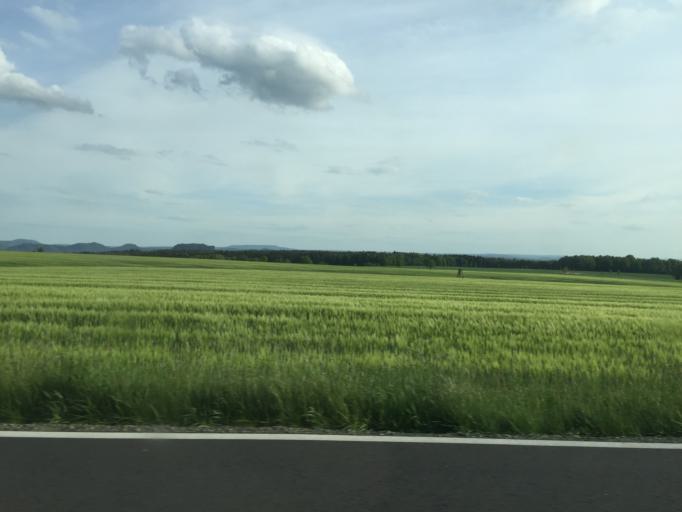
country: DE
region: Saxony
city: Stadt Wehlen
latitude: 50.9881
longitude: 14.0612
